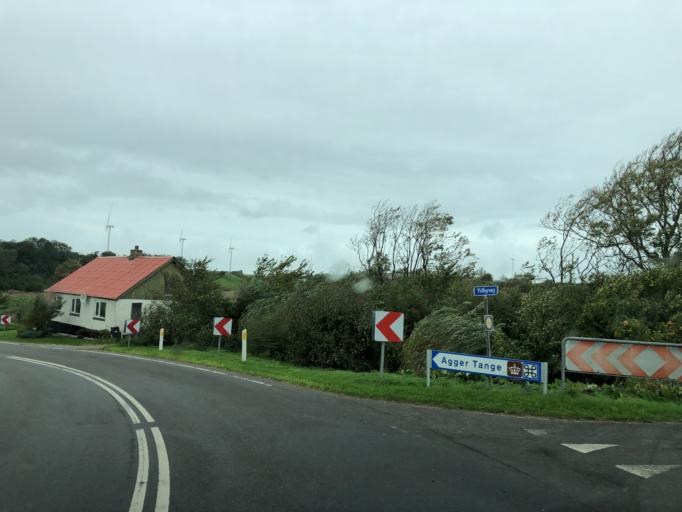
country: DK
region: North Denmark
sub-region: Thisted Kommune
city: Hurup
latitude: 56.7188
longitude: 8.3889
